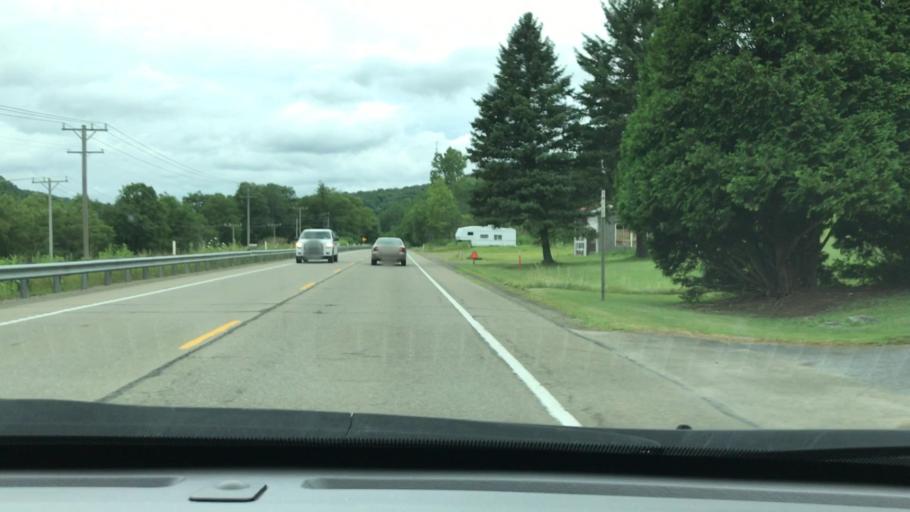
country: US
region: Pennsylvania
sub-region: Elk County
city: Johnsonburg
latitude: 41.5514
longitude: -78.6830
